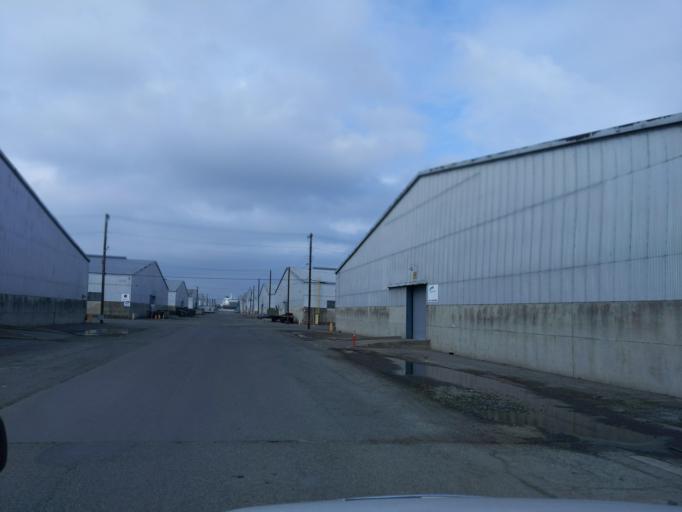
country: US
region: California
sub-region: San Joaquin County
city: Country Club
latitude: 37.9522
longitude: -121.3635
